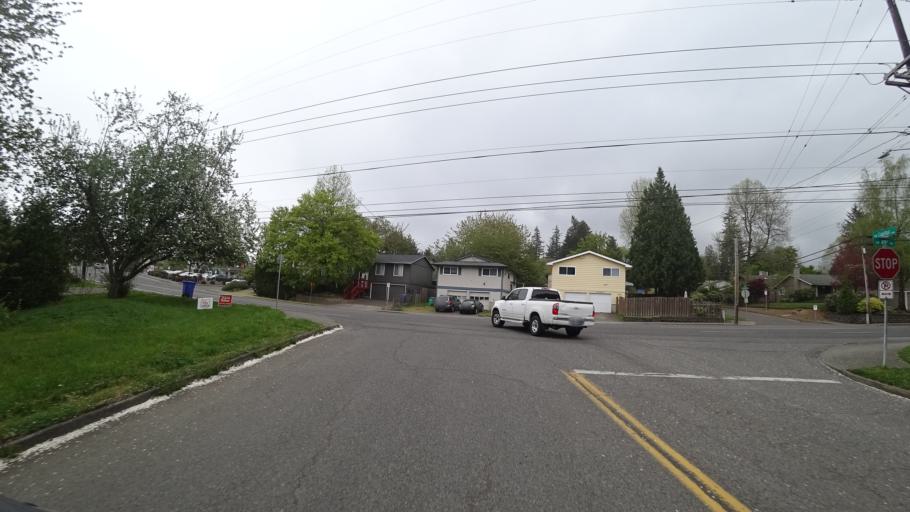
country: US
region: Oregon
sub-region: Washington County
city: Metzger
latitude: 45.4442
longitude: -122.7274
